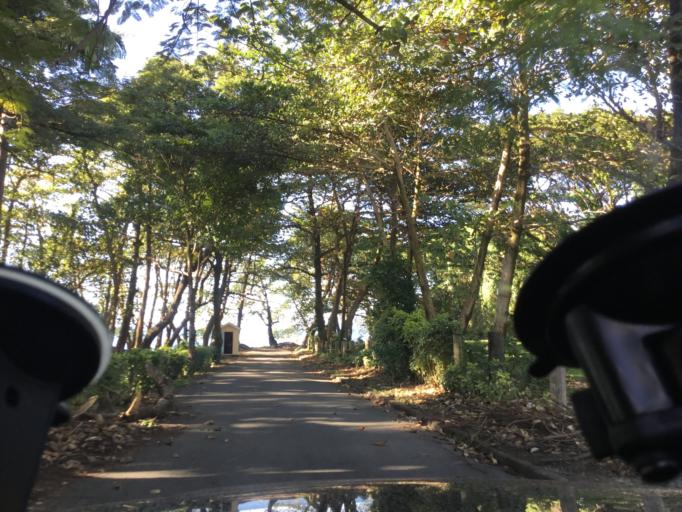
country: VC
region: Saint David
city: Chateaubelair
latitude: 13.3102
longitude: -61.2341
